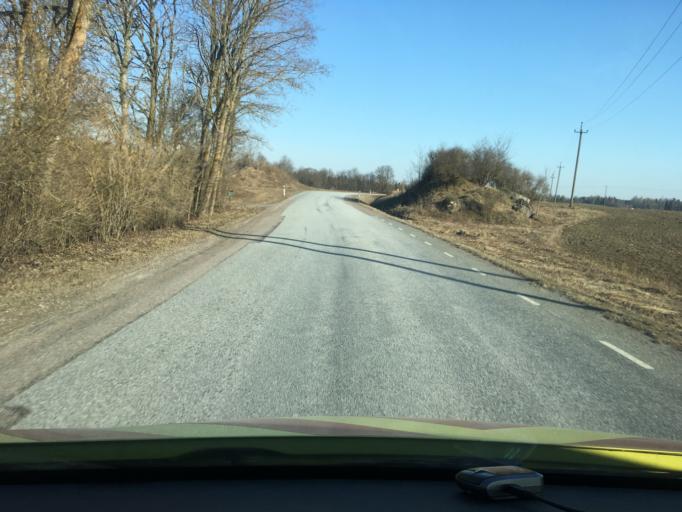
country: EE
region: Raplamaa
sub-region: Rapla vald
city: Rapla
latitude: 59.0309
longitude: 24.8365
